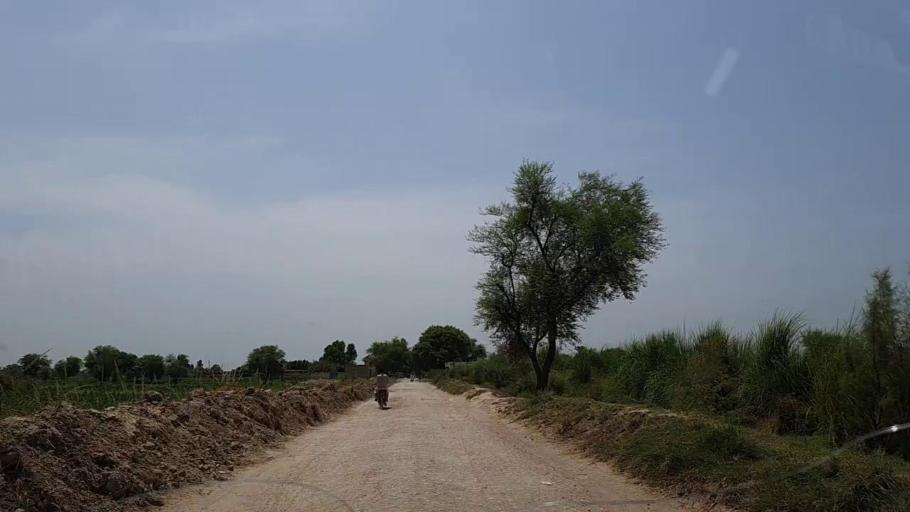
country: PK
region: Sindh
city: Khanpur
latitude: 27.8540
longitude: 69.4862
